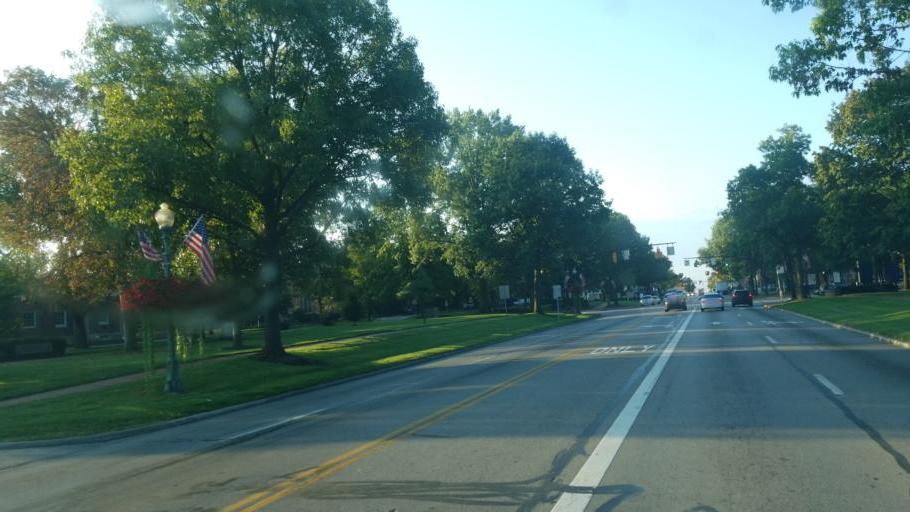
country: US
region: Ohio
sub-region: Franklin County
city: Worthington
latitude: 40.0897
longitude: -83.0181
